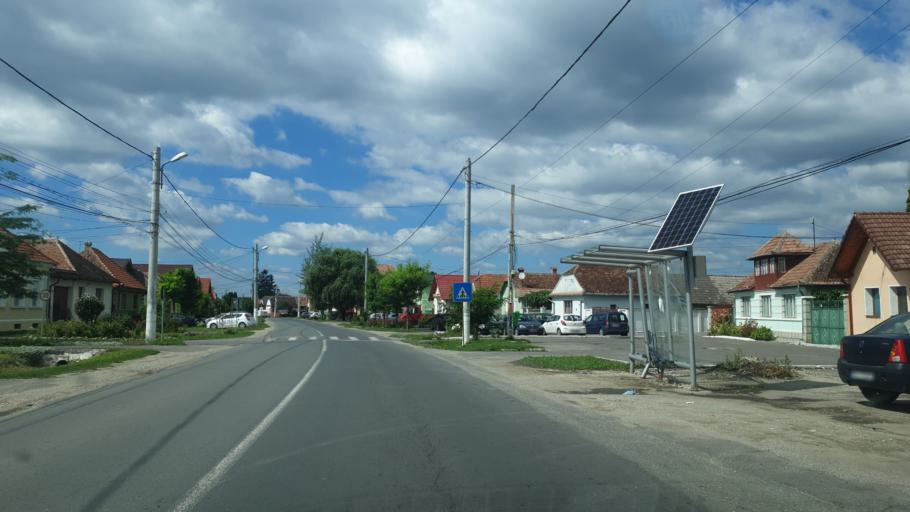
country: RO
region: Brasov
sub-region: Comuna Sanpetru
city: Sanpetru
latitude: 45.7160
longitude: 25.6297
